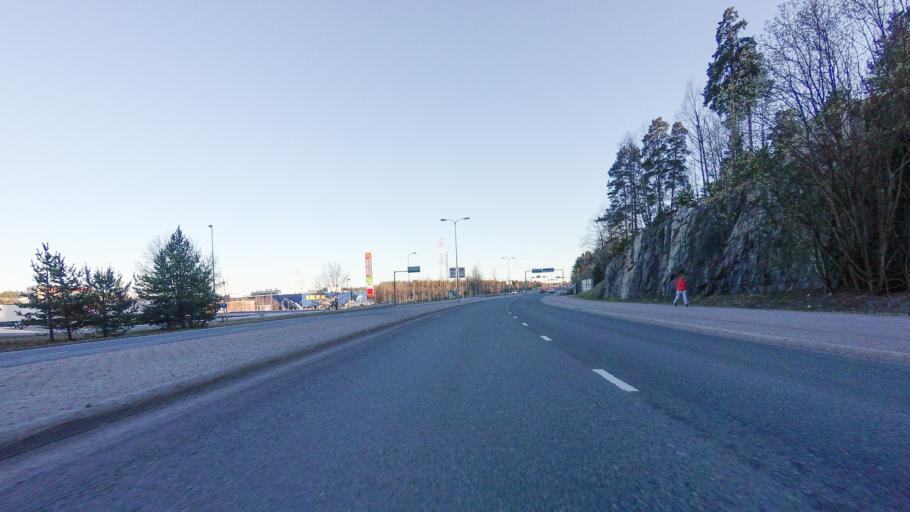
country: FI
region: Uusimaa
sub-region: Helsinki
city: Vantaa
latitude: 60.2807
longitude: 25.0799
